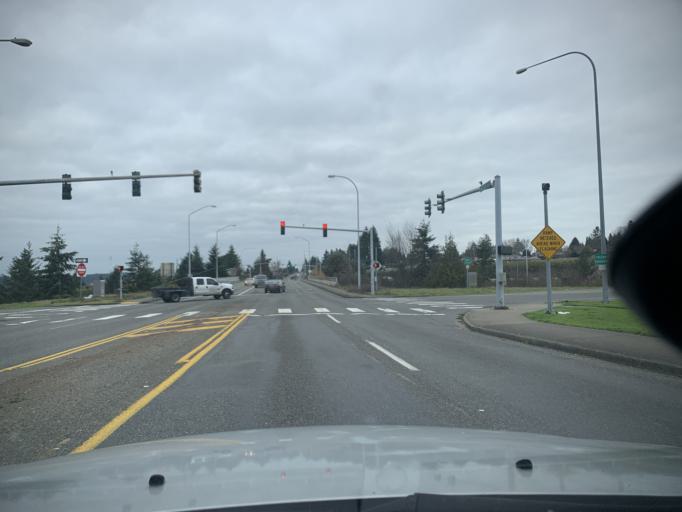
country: US
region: Washington
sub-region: Pierce County
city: University Place
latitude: 47.2577
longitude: -122.5370
